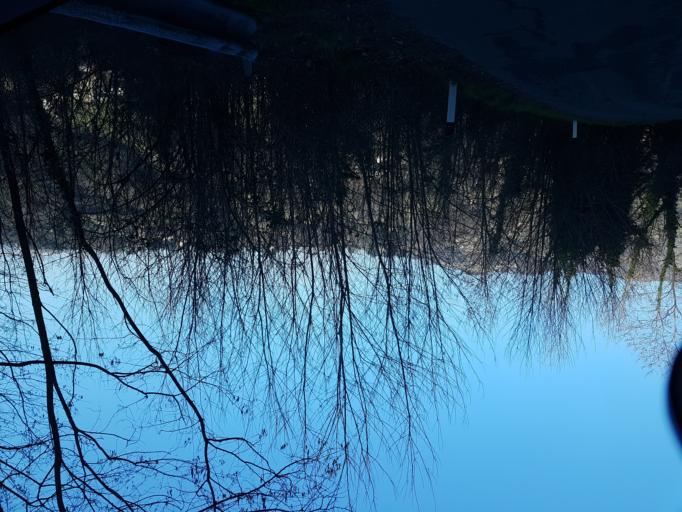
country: IT
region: Liguria
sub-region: Provincia di Genova
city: Campomorone
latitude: 44.5107
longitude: 8.8748
